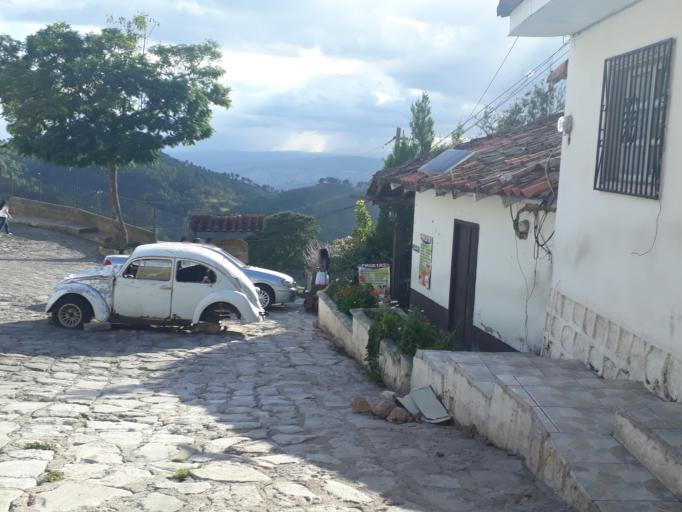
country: HN
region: Francisco Morazan
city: Santa Lucia
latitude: 14.1146
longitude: -87.1137
